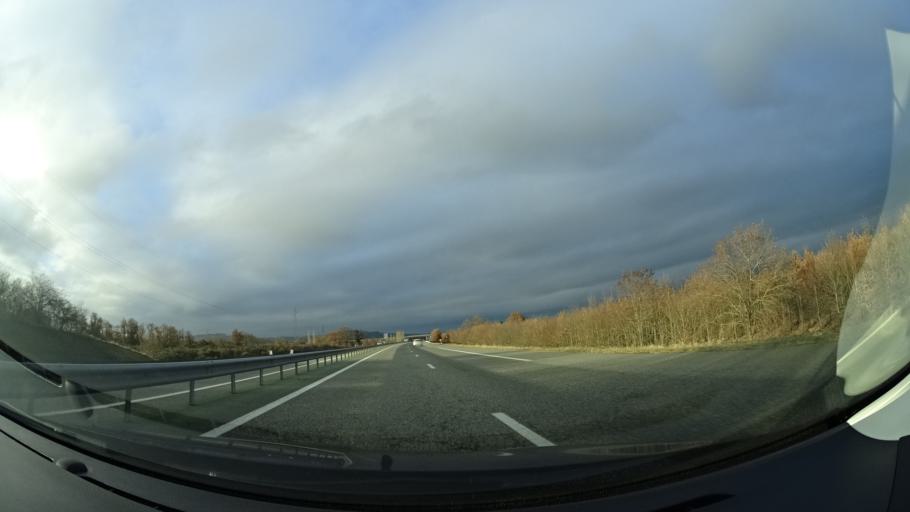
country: FR
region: Midi-Pyrenees
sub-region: Departement de l'Ariege
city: Pamiers
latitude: 43.1428
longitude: 1.6208
